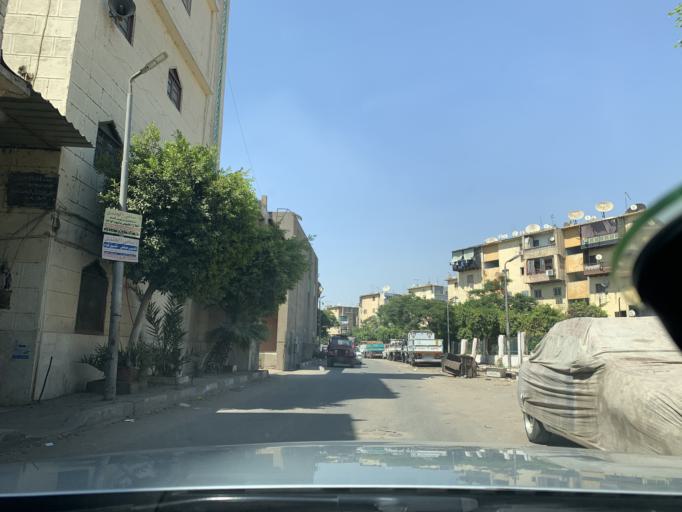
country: EG
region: Muhafazat al Qahirah
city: Cairo
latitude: 30.0719
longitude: 31.2562
